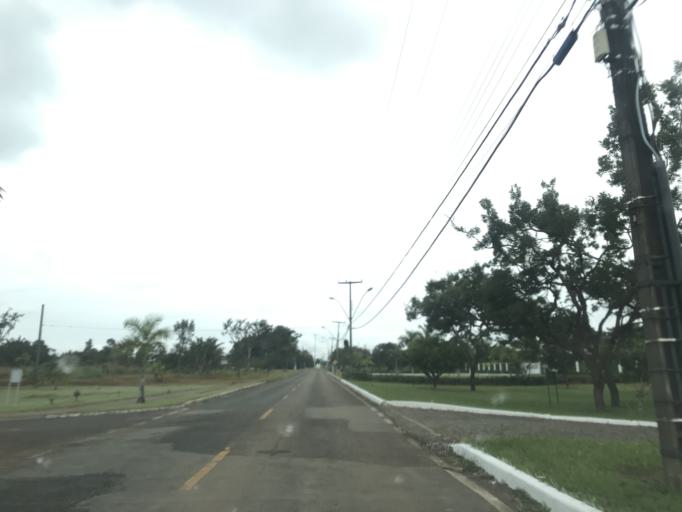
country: BR
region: Federal District
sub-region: Brasilia
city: Brasilia
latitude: -15.8958
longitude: -47.9317
